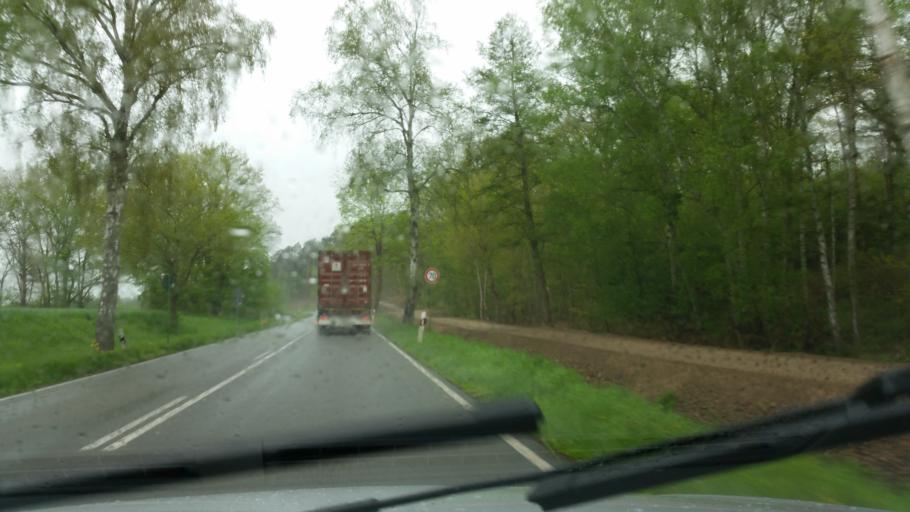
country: DE
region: Saxony-Anhalt
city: Kalbe
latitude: 52.6256
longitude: 11.3135
